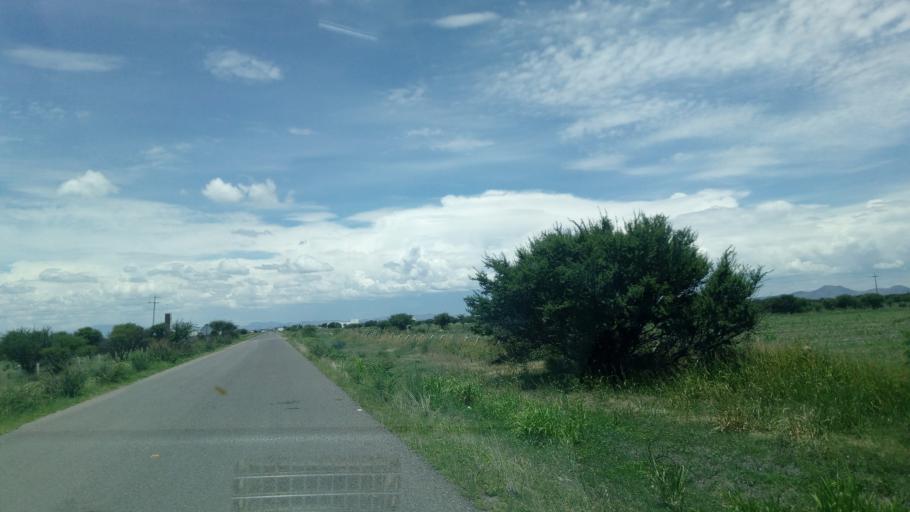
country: MX
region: Durango
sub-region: Durango
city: Jose Refugio Salcido
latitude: 24.1594
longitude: -104.5063
